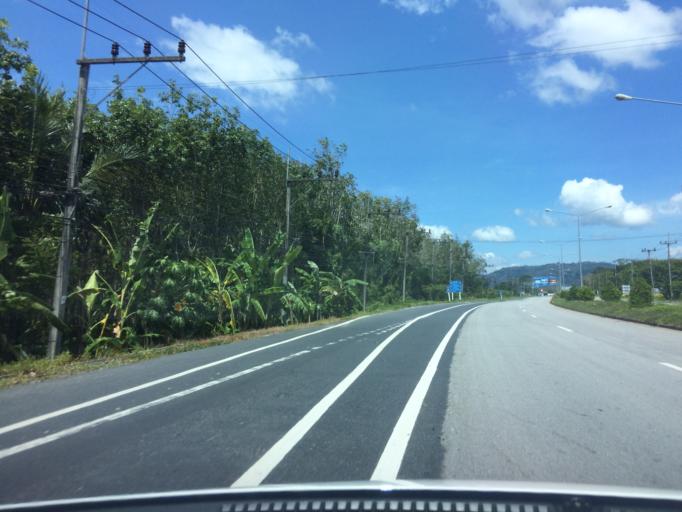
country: TH
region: Phangnga
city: Thai Mueang
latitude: 8.2472
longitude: 98.2977
